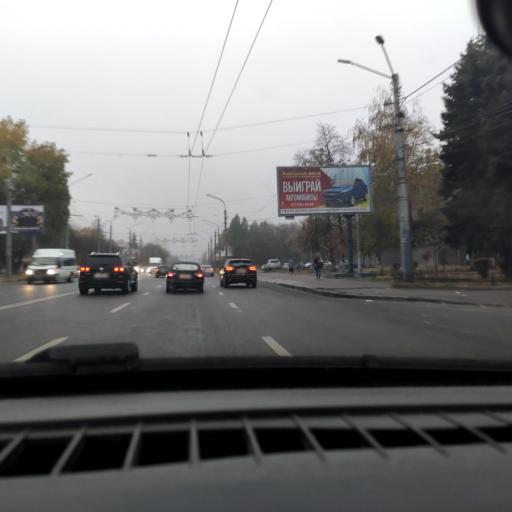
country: RU
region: Voronezj
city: Voronezh
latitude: 51.6527
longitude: 39.1686
